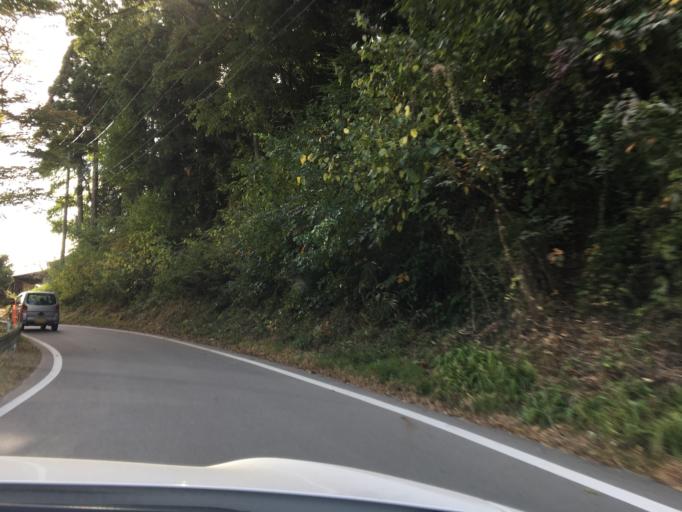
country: JP
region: Fukushima
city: Nihommatsu
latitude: 37.5307
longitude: 140.5066
